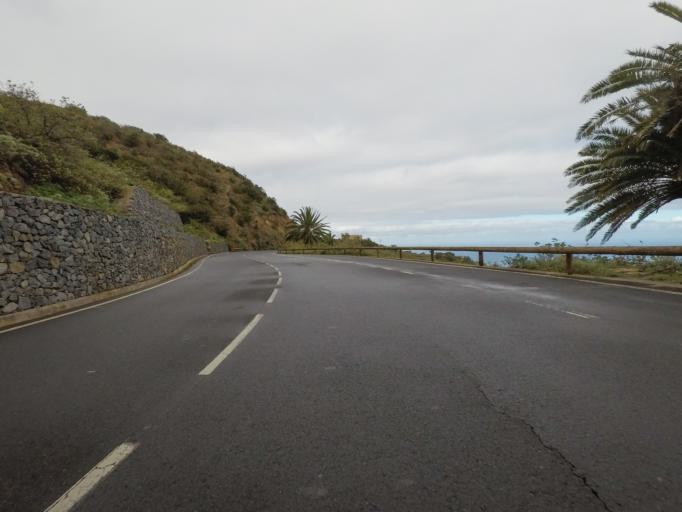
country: ES
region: Canary Islands
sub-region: Provincia de Santa Cruz de Tenerife
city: Agulo
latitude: 28.1904
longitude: -17.2275
